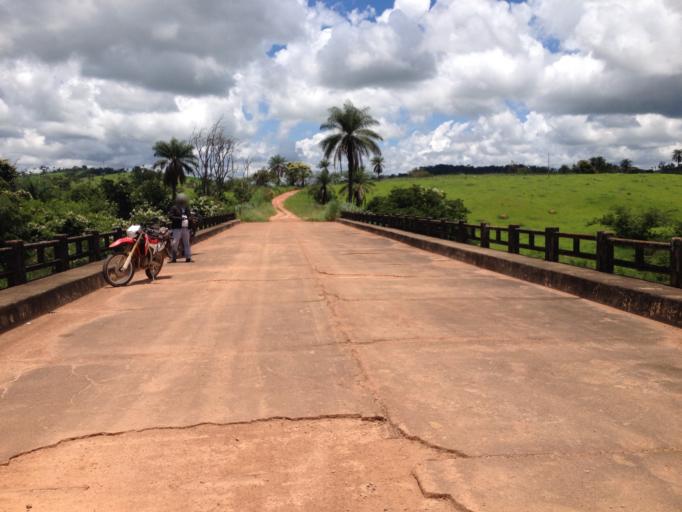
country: BR
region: Minas Gerais
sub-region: Monte Carmelo
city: Monte Carmelo
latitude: -18.6267
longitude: -47.7041
